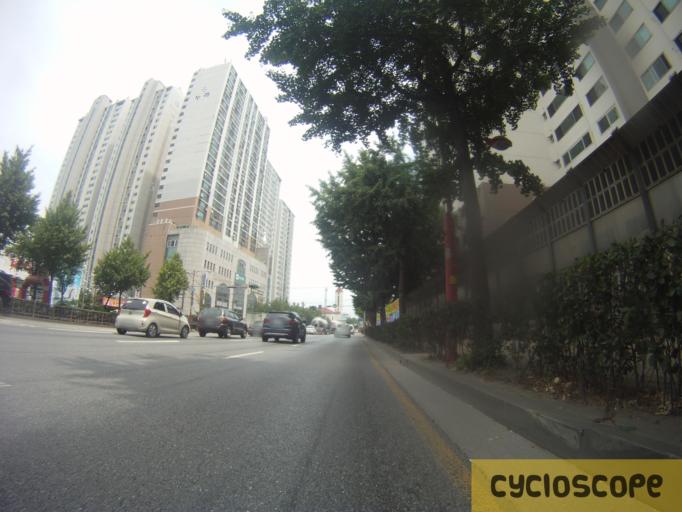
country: KR
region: Incheon
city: Incheon
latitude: 37.4653
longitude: 126.6335
